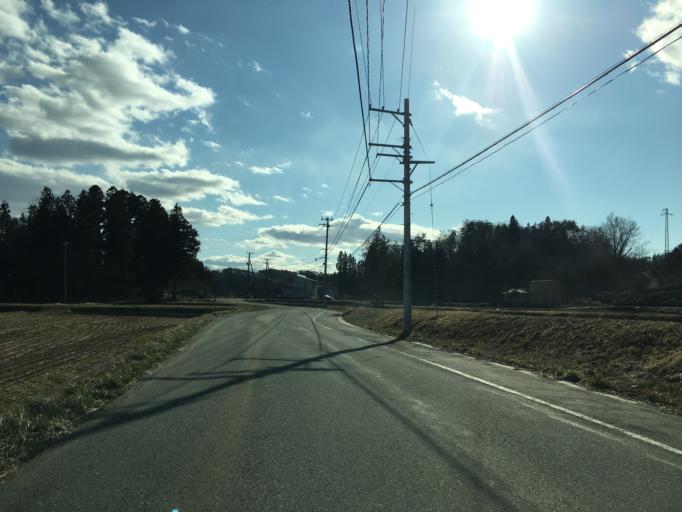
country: JP
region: Yamagata
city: Nagai
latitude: 37.9969
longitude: 140.0109
